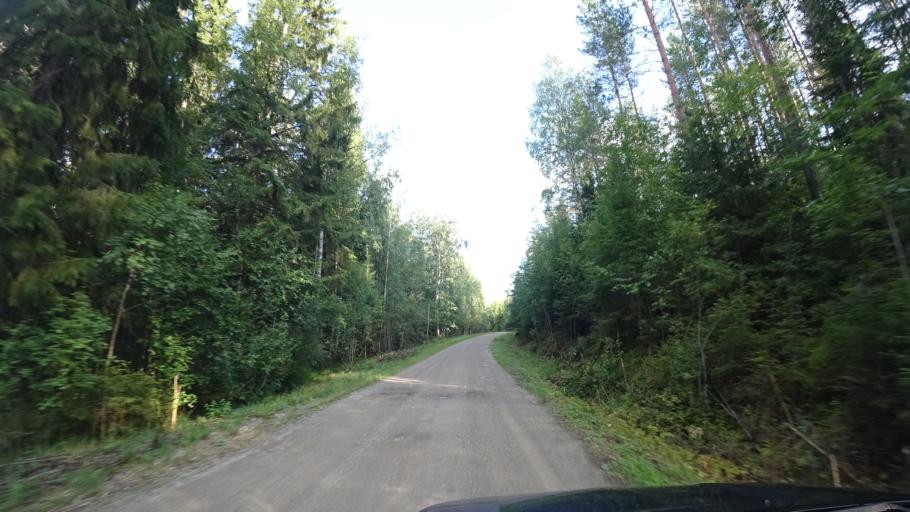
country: FI
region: Paijanne Tavastia
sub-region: Lahti
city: Auttoinen
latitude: 61.2136
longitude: 25.1598
